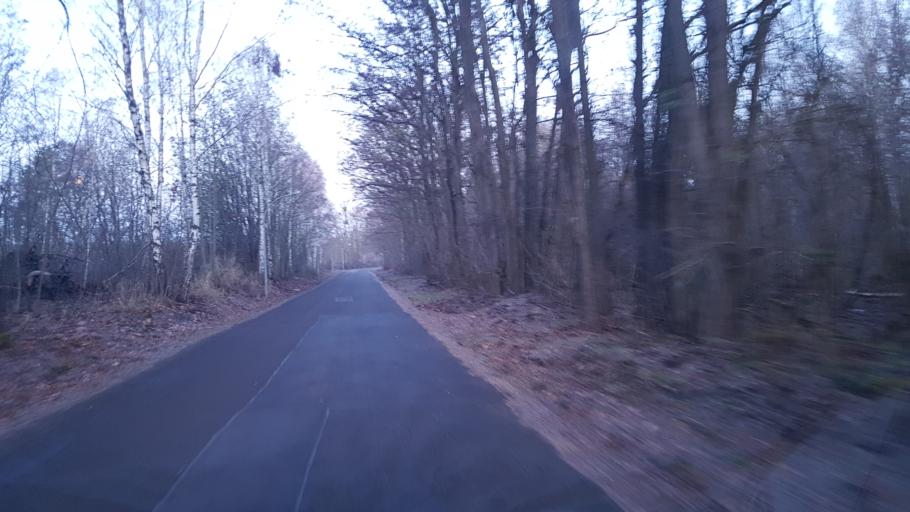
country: DE
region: Brandenburg
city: Schipkau
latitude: 51.5448
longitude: 13.8873
